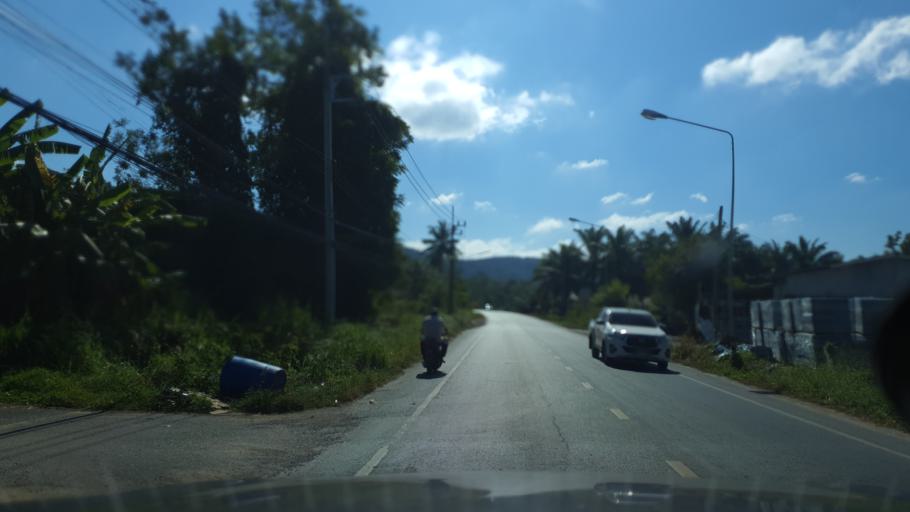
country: TH
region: Phangnga
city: Ban Ao Nang
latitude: 8.0646
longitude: 98.8102
